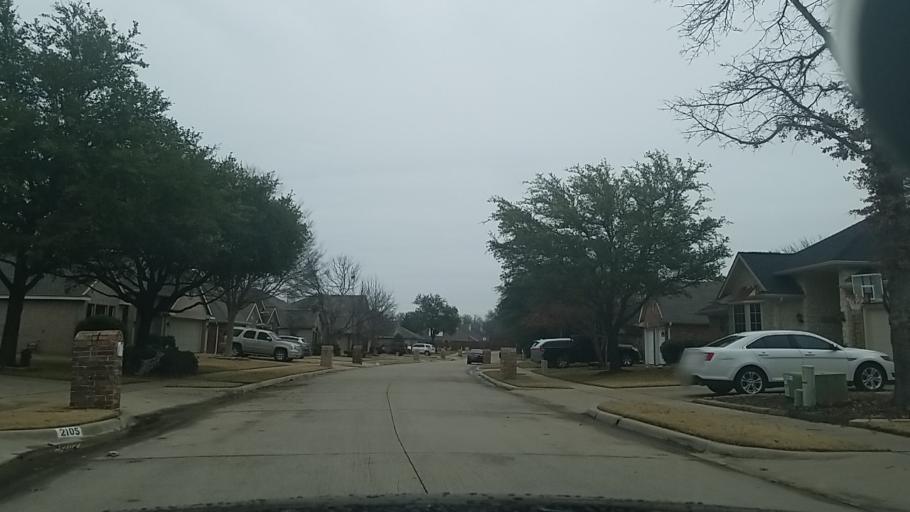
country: US
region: Texas
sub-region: Denton County
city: Corinth
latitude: 33.1589
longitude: -97.0789
